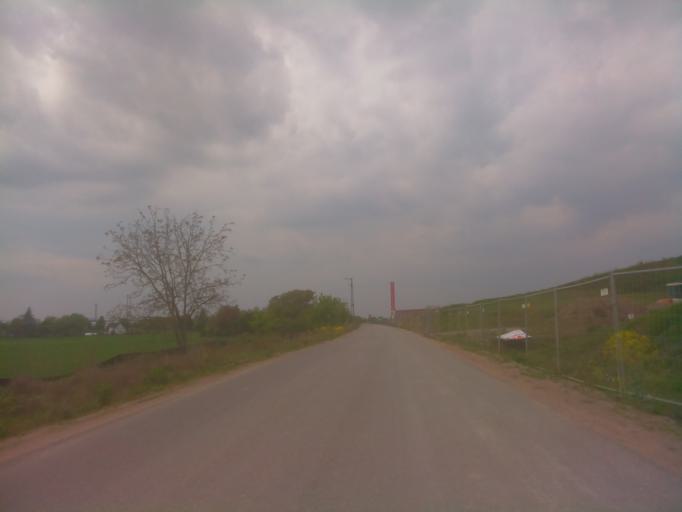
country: DE
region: Baden-Wuerttemberg
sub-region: Karlsruhe Region
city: Eppelheim
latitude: 49.4041
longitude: 8.6600
